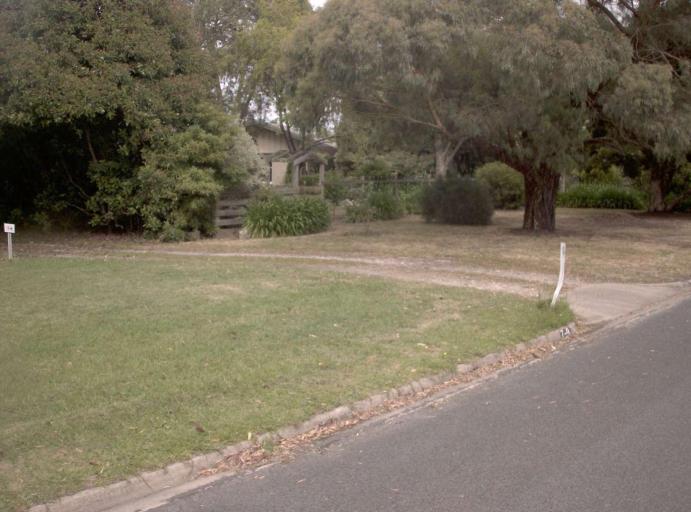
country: AU
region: Victoria
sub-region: Latrobe
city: Moe
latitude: -38.0736
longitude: 146.1796
